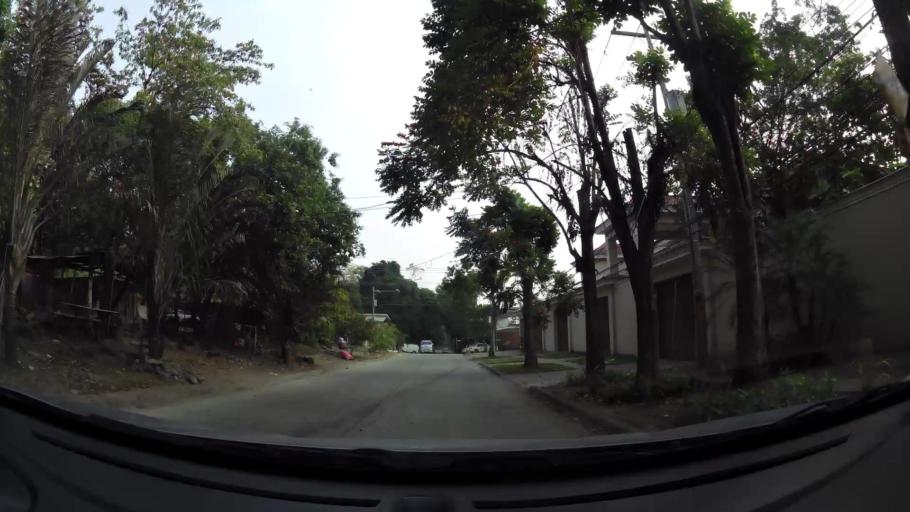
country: HN
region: Cortes
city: Armenta
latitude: 15.5042
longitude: -88.0473
